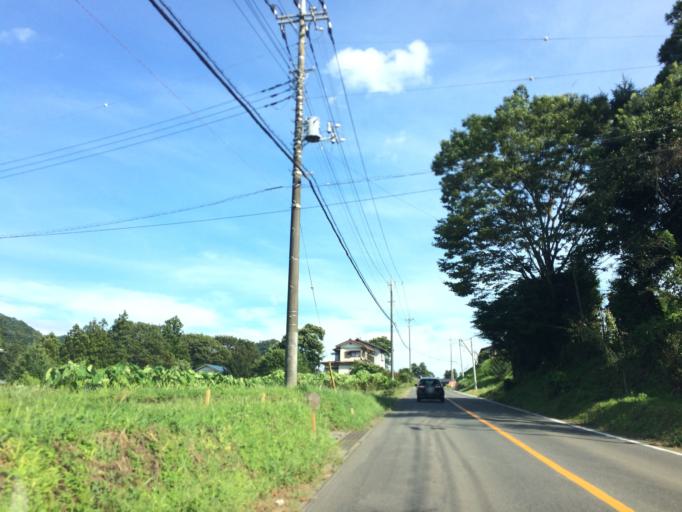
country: JP
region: Gunma
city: Nakanojomachi
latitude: 36.5646
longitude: 138.8861
